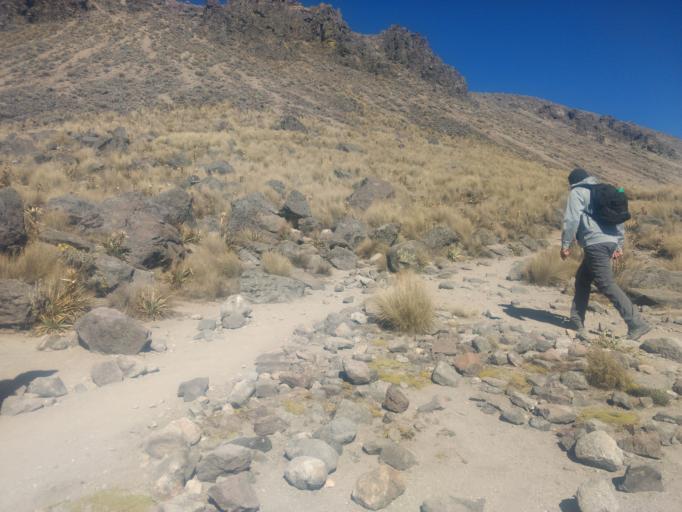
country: MX
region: Mexico
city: Cerro La Calera
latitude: 19.1123
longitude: -99.7550
